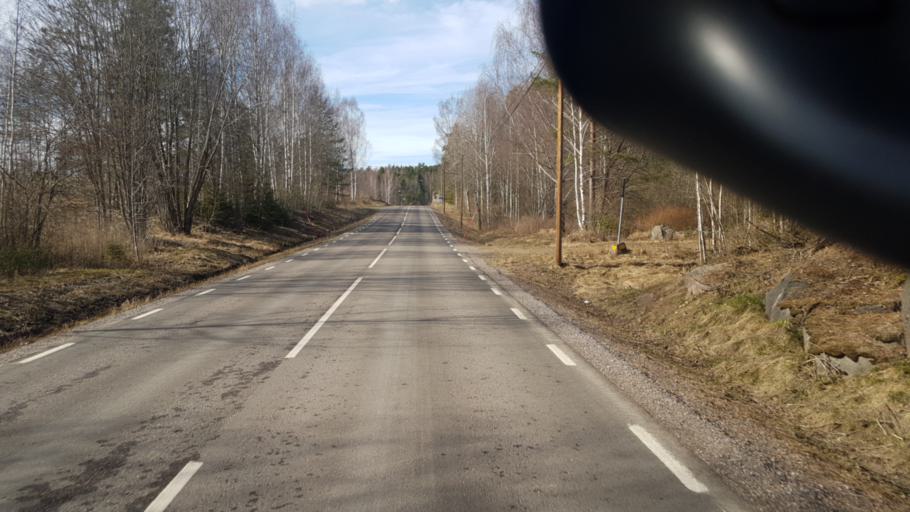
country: SE
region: Vaermland
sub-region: Eda Kommun
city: Amotfors
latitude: 59.7548
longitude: 12.3622
